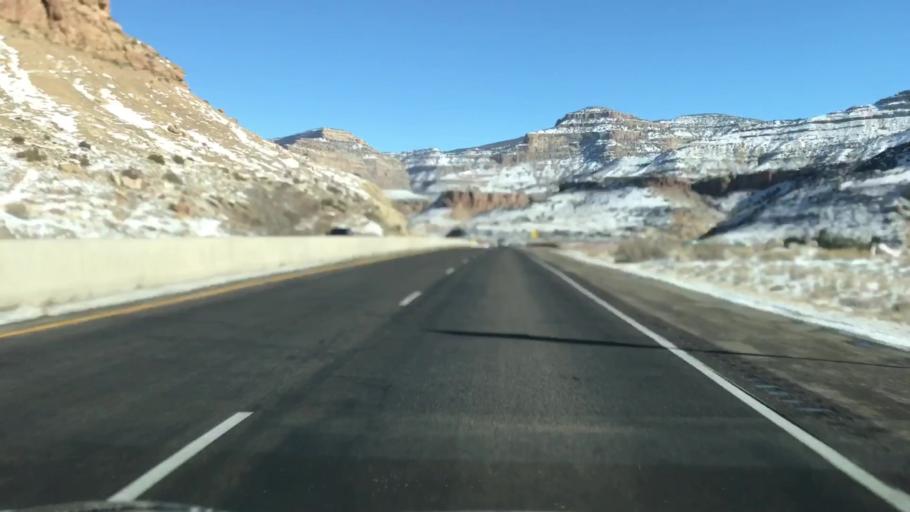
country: US
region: Colorado
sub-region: Mesa County
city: Palisade
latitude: 39.1188
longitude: -108.3274
